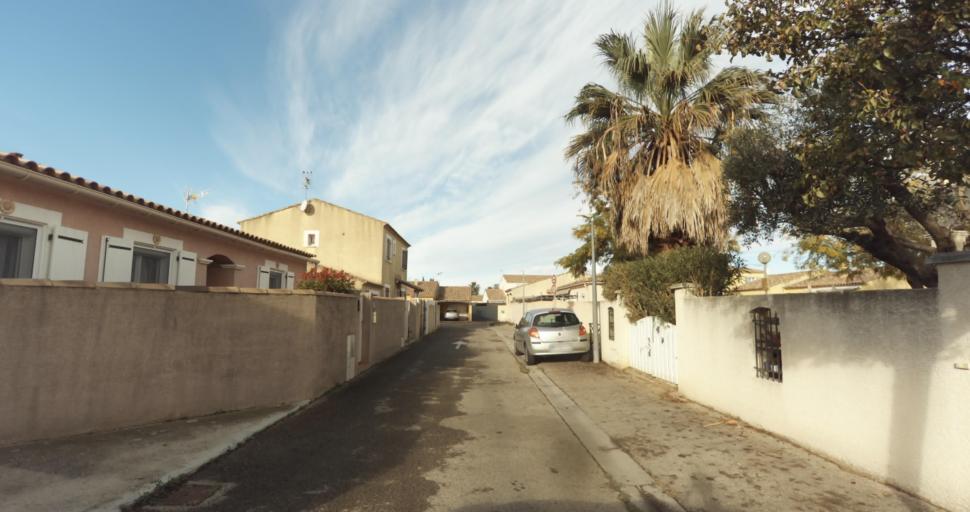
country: FR
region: Languedoc-Roussillon
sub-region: Departement du Gard
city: Aigues-Mortes
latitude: 43.5663
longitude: 4.2055
